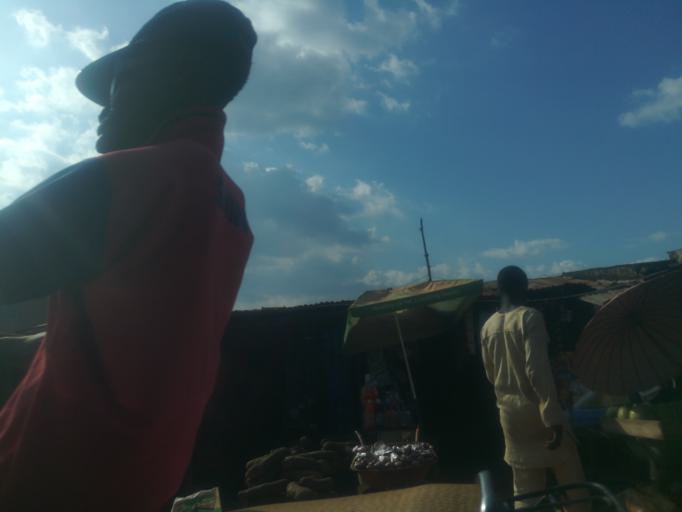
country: NG
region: Oyo
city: Ibadan
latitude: 7.3906
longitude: 3.9741
